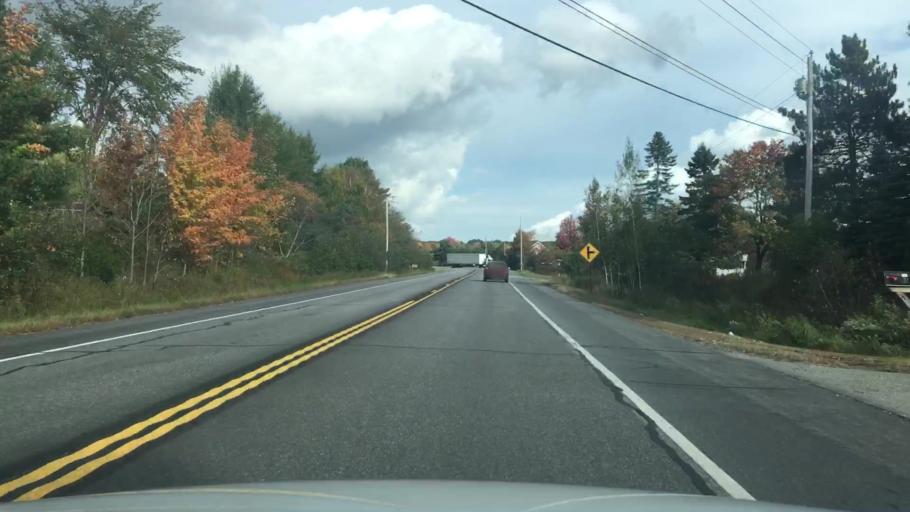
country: US
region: Maine
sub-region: Knox County
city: Rockland
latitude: 44.1518
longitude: -69.1146
